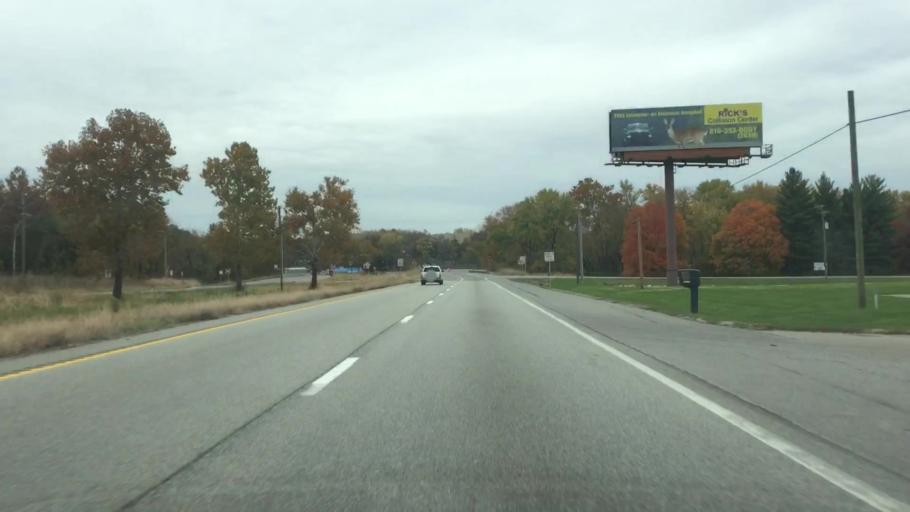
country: US
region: Missouri
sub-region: Jackson County
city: Raytown
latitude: 38.9622
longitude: -94.4250
